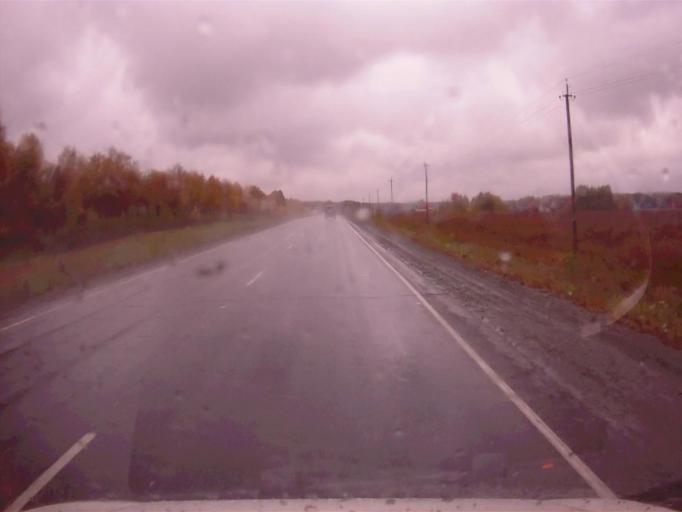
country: RU
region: Chelyabinsk
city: Argayash
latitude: 55.4051
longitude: 61.0618
